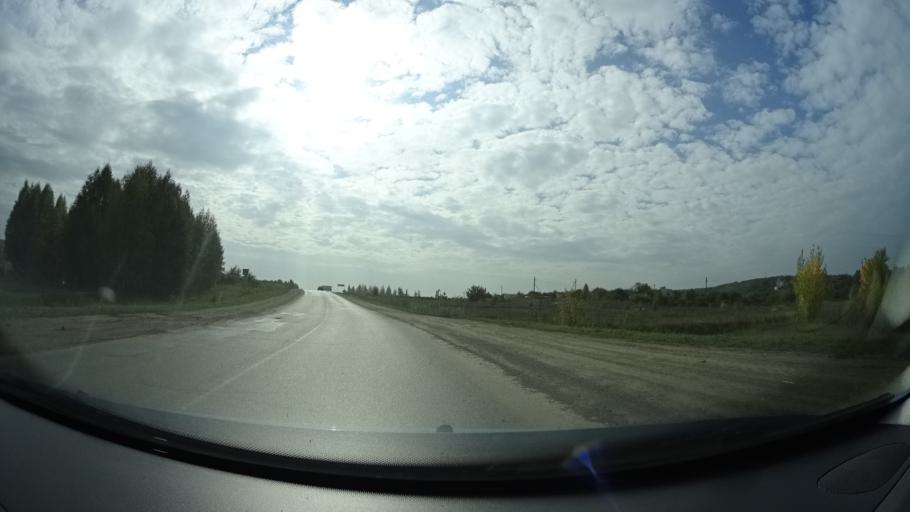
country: RU
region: Bashkortostan
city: Oktyabr'skiy
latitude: 54.5437
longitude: 53.5676
